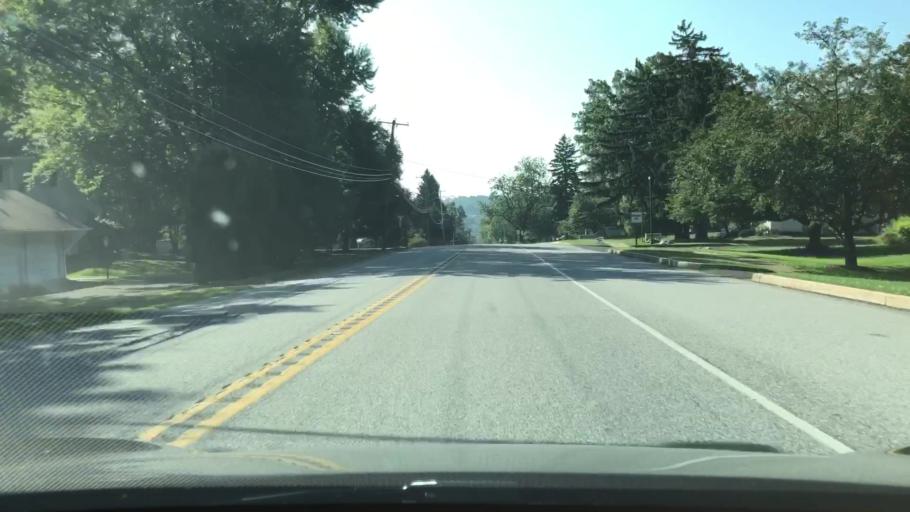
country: US
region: Pennsylvania
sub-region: Montgomery County
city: Dresher
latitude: 40.1497
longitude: -75.1705
